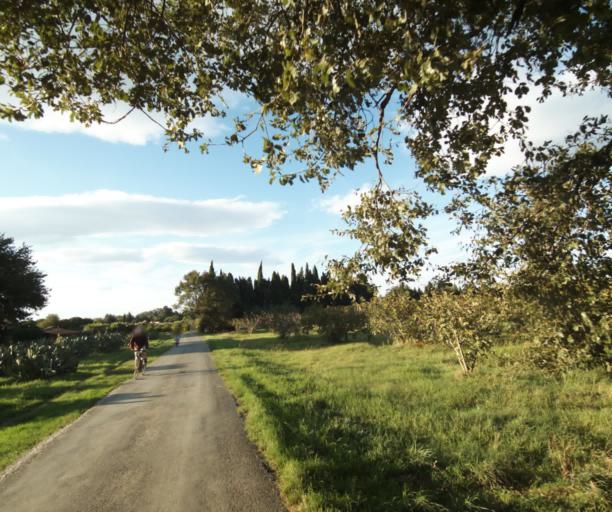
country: FR
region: Languedoc-Roussillon
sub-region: Departement des Pyrenees-Orientales
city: Latour-Bas-Elne
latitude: 42.5799
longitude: 3.0131
